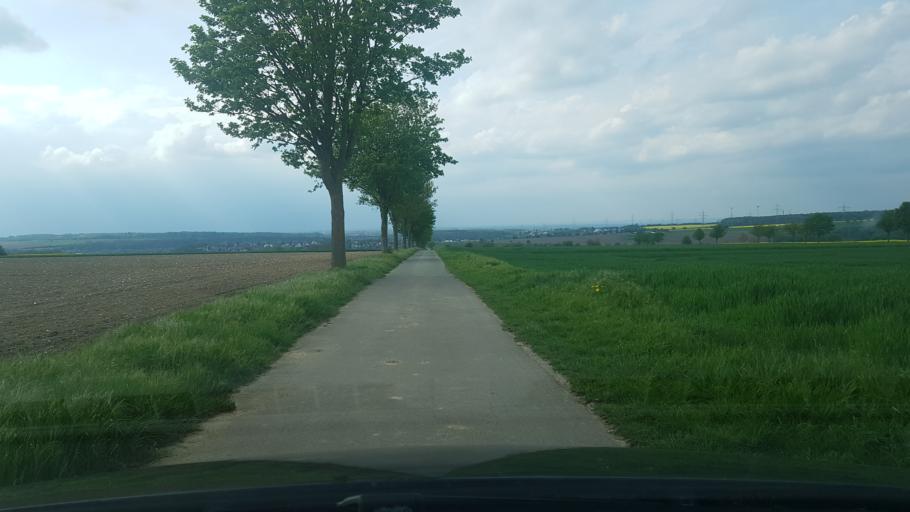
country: DE
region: North Rhine-Westphalia
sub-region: Regierungsbezirk Detmold
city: Paderborn
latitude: 51.6516
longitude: 8.7505
